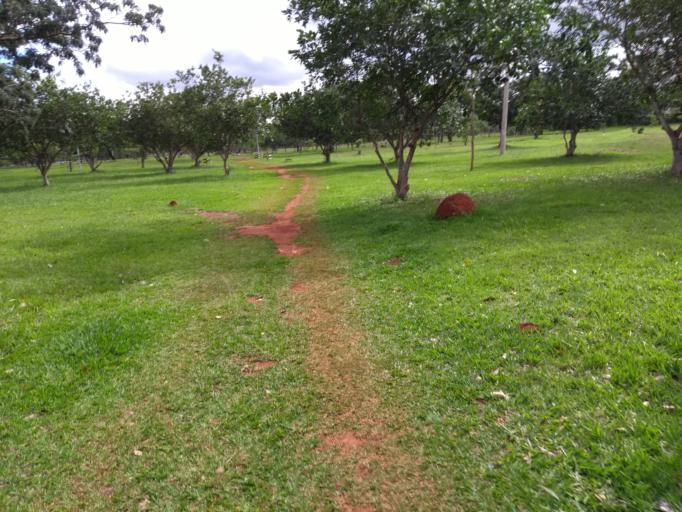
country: BR
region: Federal District
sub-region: Brasilia
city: Brasilia
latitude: -15.8038
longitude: -47.9418
